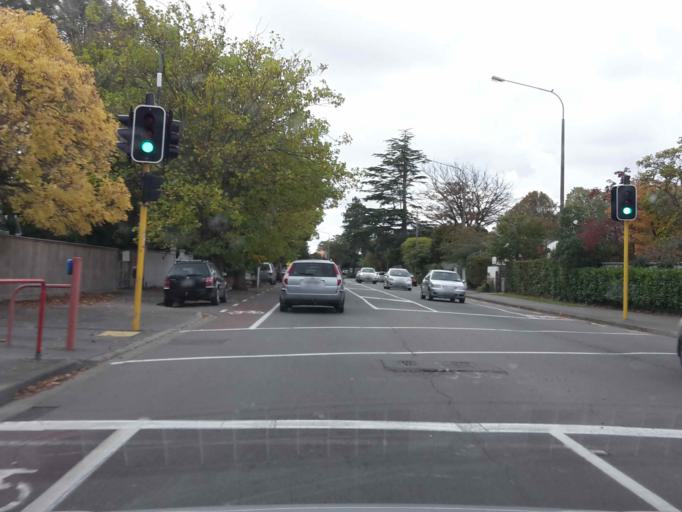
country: NZ
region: Canterbury
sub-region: Christchurch City
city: Christchurch
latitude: -43.5259
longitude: 172.6022
